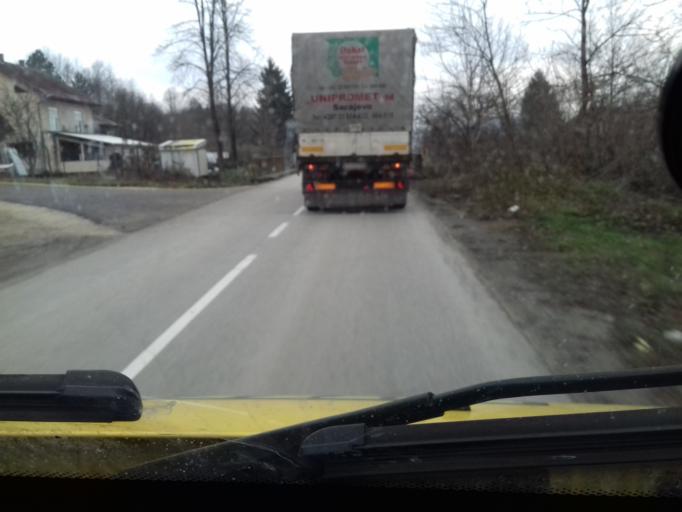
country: BA
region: Federation of Bosnia and Herzegovina
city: Dubravica
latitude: 44.4205
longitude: 18.0905
